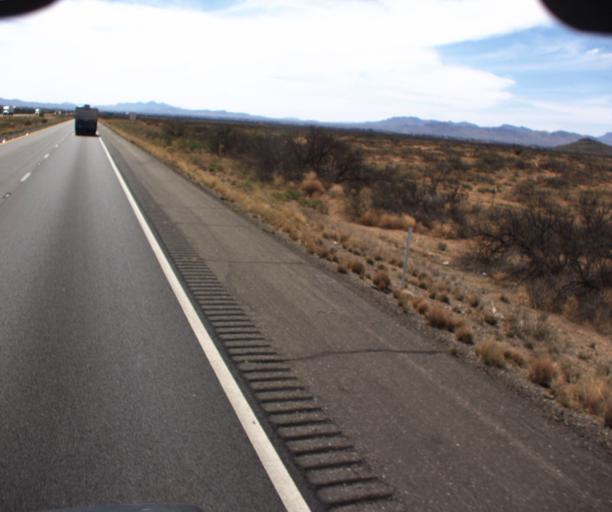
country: US
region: Arizona
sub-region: Cochise County
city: Willcox
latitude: 32.3052
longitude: -109.8000
